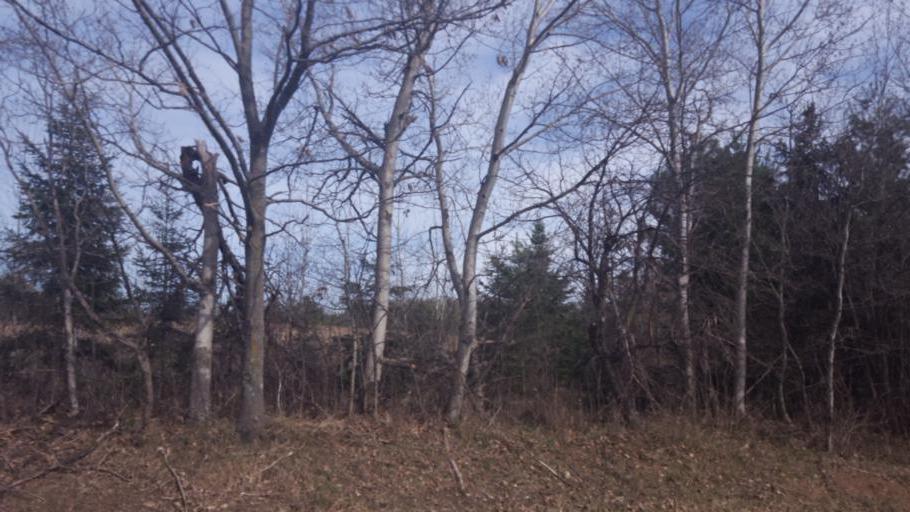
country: US
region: Michigan
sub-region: Gladwin County
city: Gladwin
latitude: 44.0227
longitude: -84.5248
